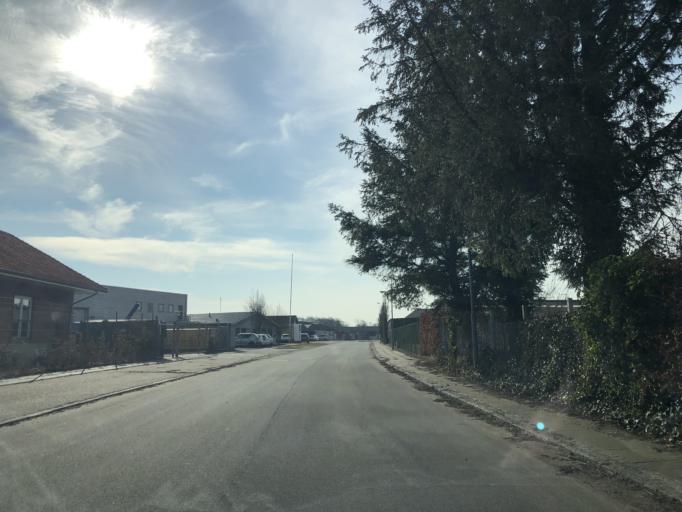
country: DK
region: Central Jutland
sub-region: Holstebro Kommune
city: Holstebro
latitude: 56.3513
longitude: 8.6142
